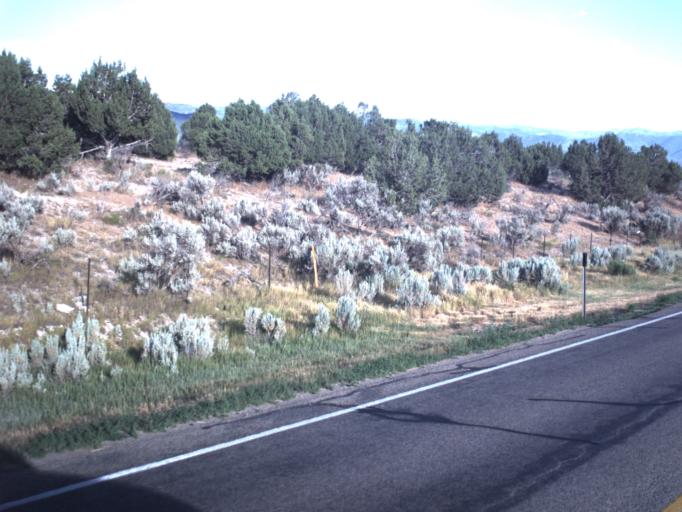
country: US
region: Utah
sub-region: Sanpete County
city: Fairview
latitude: 39.6423
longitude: -111.4492
